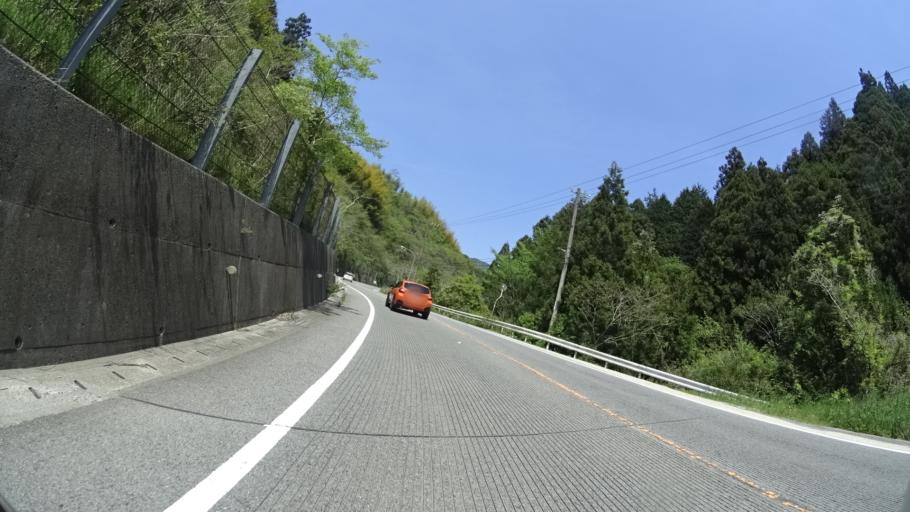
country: JP
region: Ehime
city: Hojo
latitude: 33.9242
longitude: 132.8894
